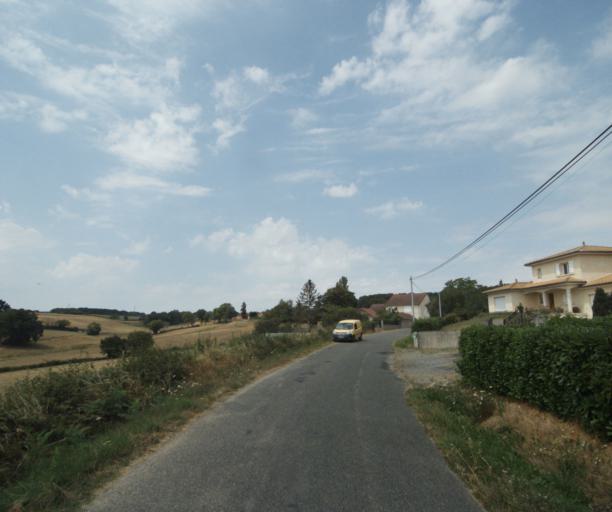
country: FR
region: Bourgogne
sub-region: Departement de Saone-et-Loire
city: Gueugnon
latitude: 46.6010
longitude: 4.0120
